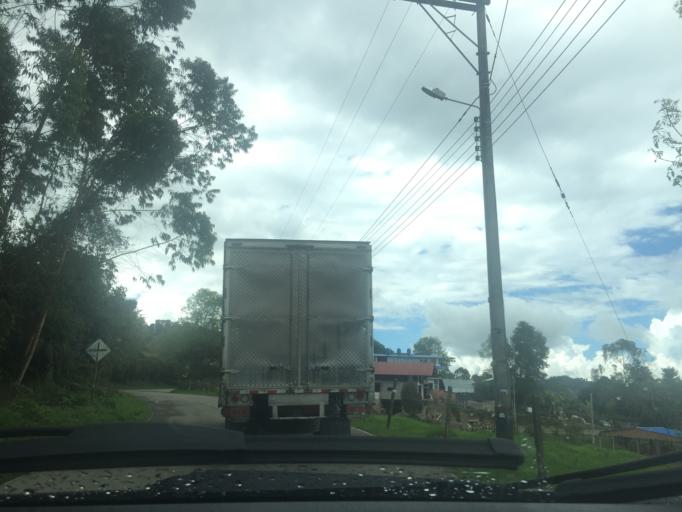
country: CO
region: Cundinamarca
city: Supata
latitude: 5.0376
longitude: -74.2667
